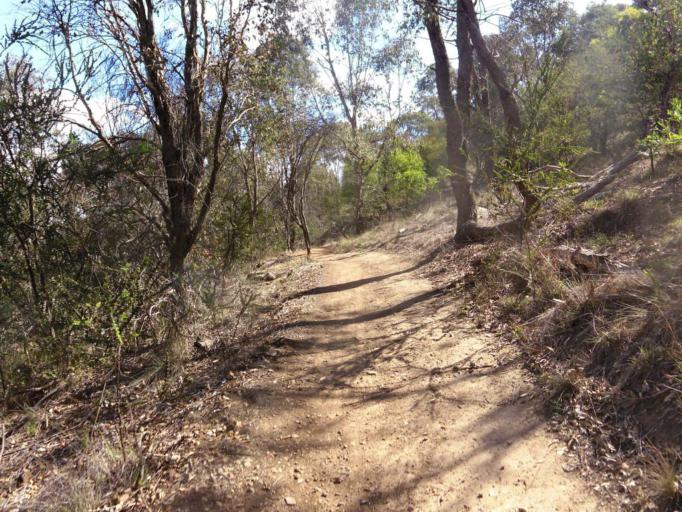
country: AU
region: Australian Capital Territory
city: Belconnen
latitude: -35.1603
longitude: 149.0758
